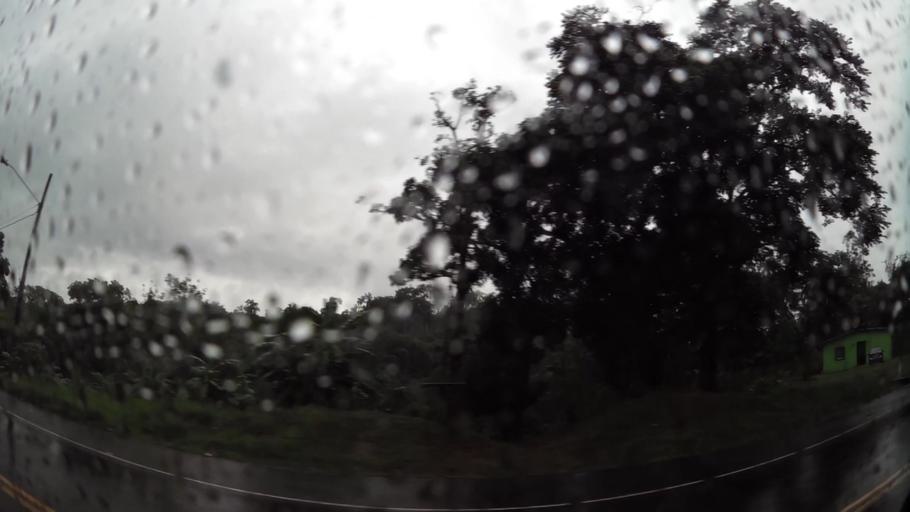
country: PA
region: Colon
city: Quebrada Bonita Adentro
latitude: 9.2869
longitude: -79.7191
